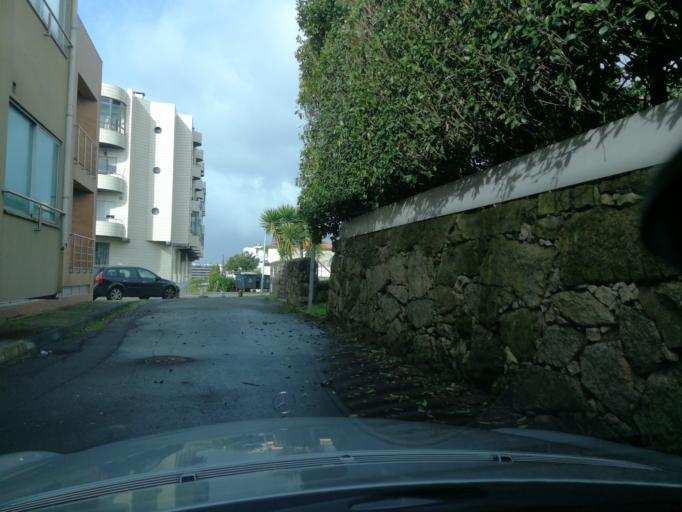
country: PT
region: Braga
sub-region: Braga
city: Braga
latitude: 41.5343
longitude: -8.4157
